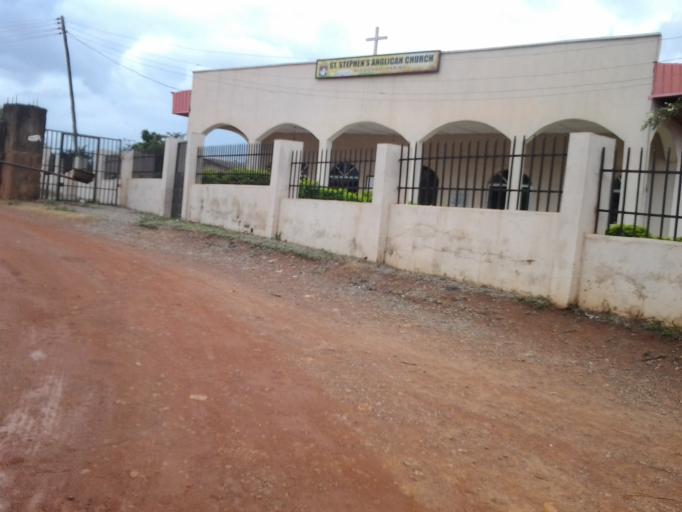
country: NG
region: Oyo
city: Ibadan
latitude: 7.4398
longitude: 3.9524
